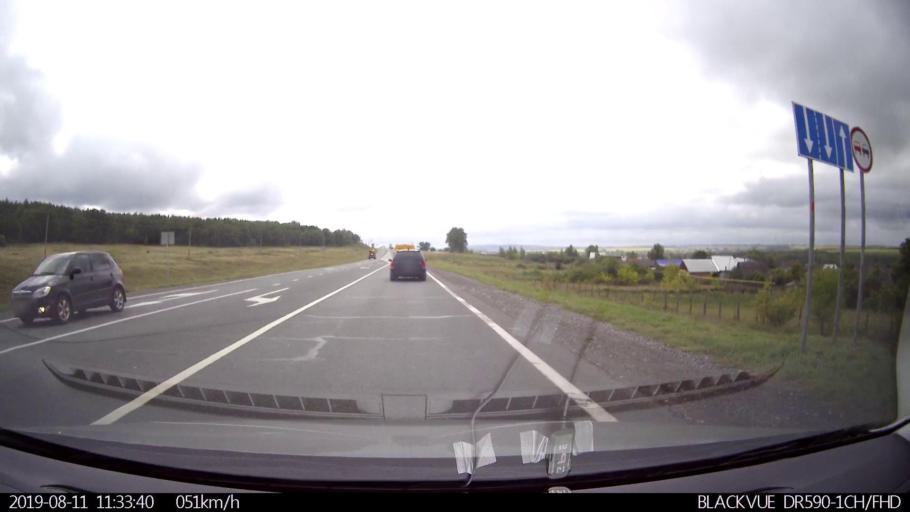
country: RU
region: Ulyanovsk
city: Silikatnyy
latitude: 54.0251
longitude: 48.2138
